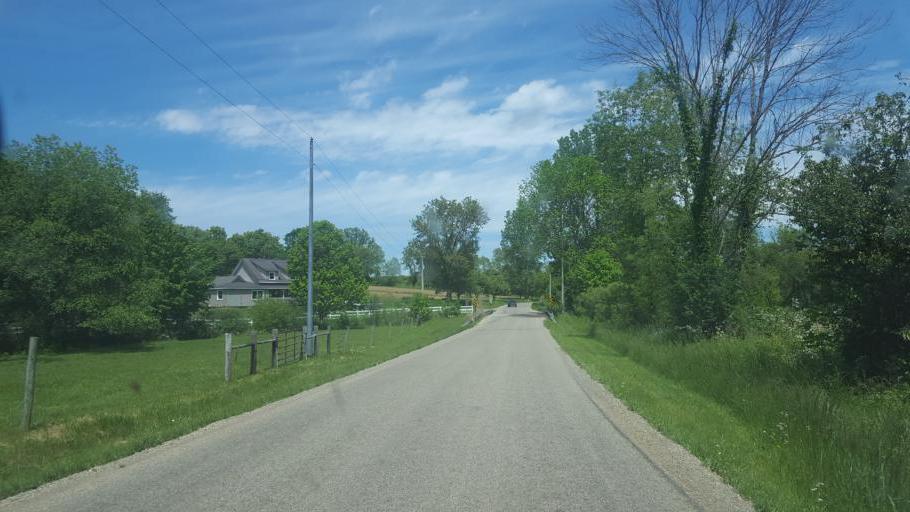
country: US
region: Ohio
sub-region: Knox County
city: Oak Hill
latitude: 40.3782
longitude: -82.3138
